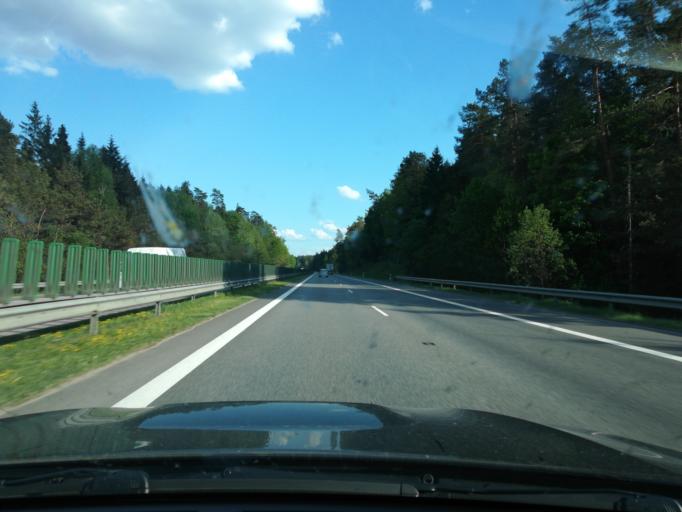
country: LT
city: Trakai
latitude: 54.7252
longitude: 24.9640
